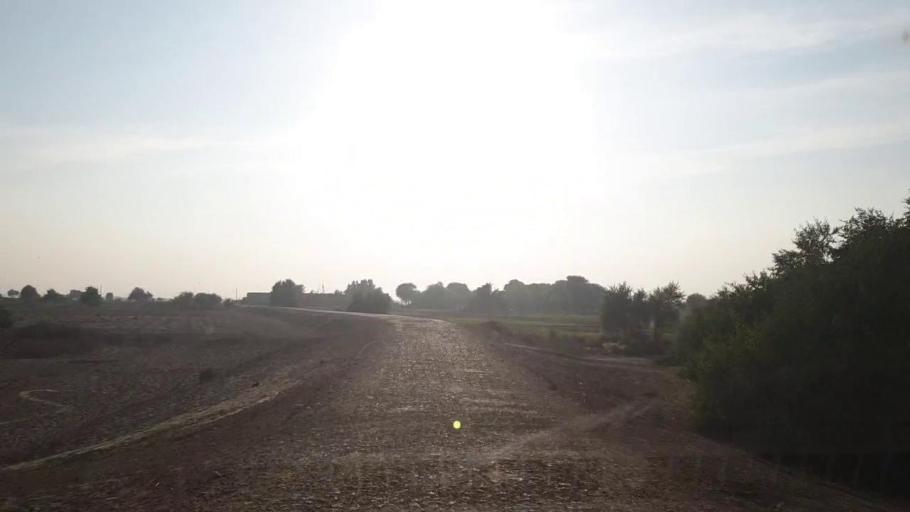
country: PK
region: Sindh
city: Sann
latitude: 25.9443
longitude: 68.1839
